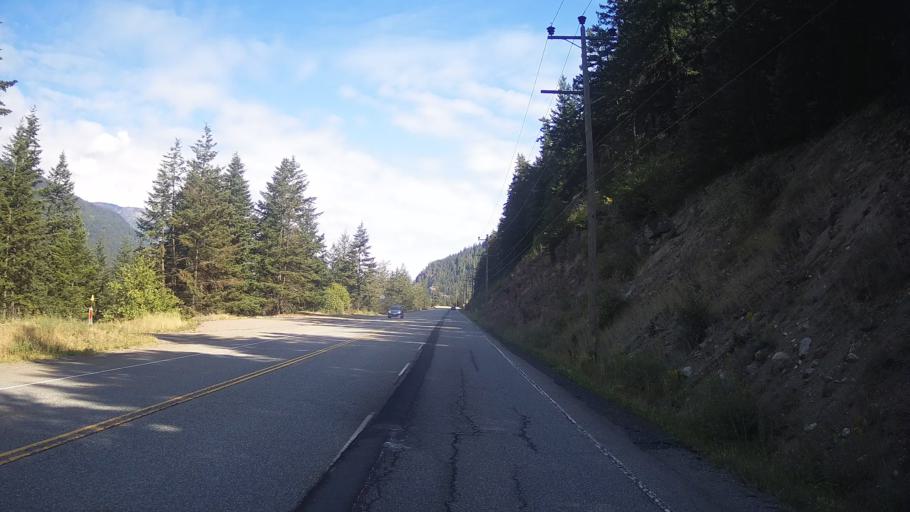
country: CA
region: British Columbia
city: Hope
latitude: 50.0581
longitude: -121.5432
